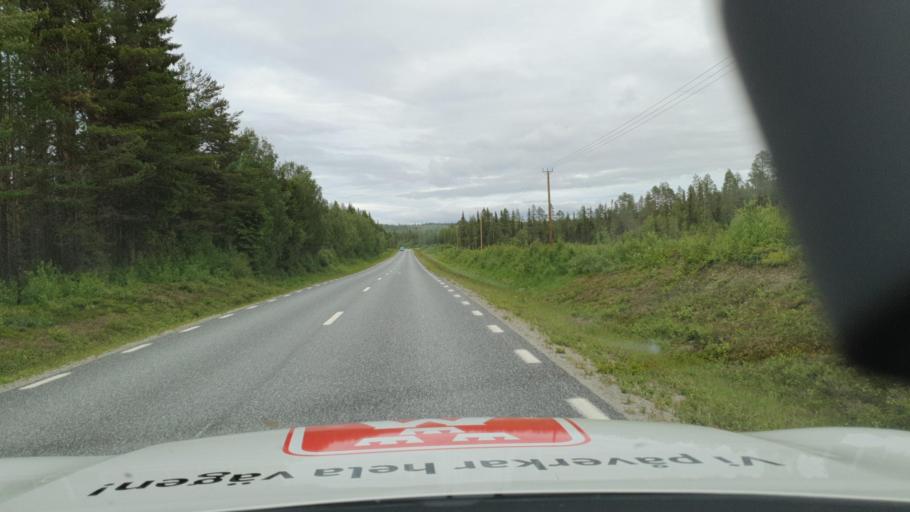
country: SE
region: Vaesterbotten
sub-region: Asele Kommun
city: Insjon
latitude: 64.3113
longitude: 17.6959
